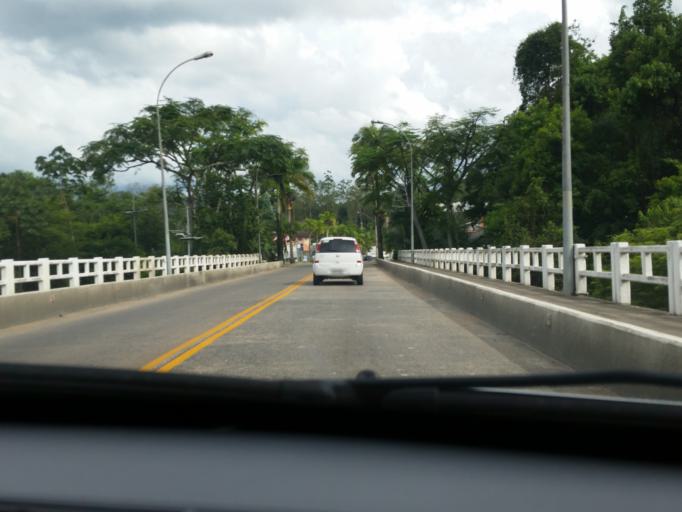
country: BR
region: Santa Catarina
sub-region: Indaial
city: Indaial
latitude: -26.8958
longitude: -49.2381
